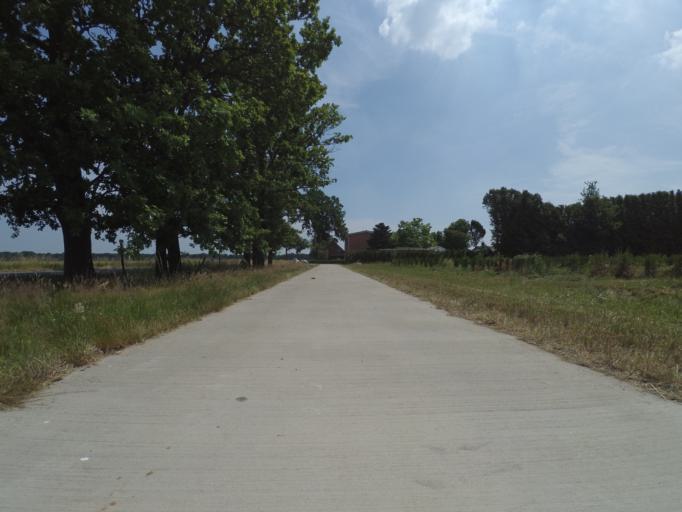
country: BE
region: Flanders
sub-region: Provincie Antwerpen
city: Wuustwezel
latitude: 51.4092
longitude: 4.5372
